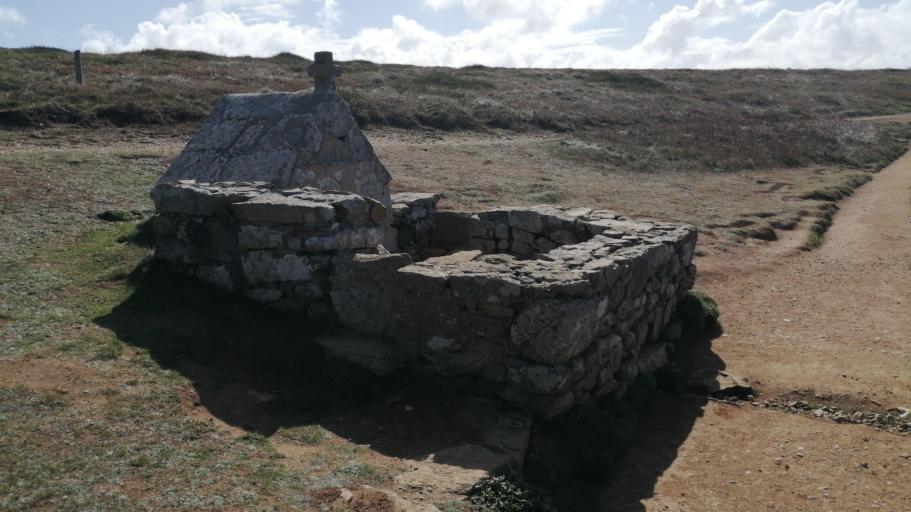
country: FR
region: Brittany
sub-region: Departement du Finistere
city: Plogoff
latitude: 48.0585
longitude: -4.7130
